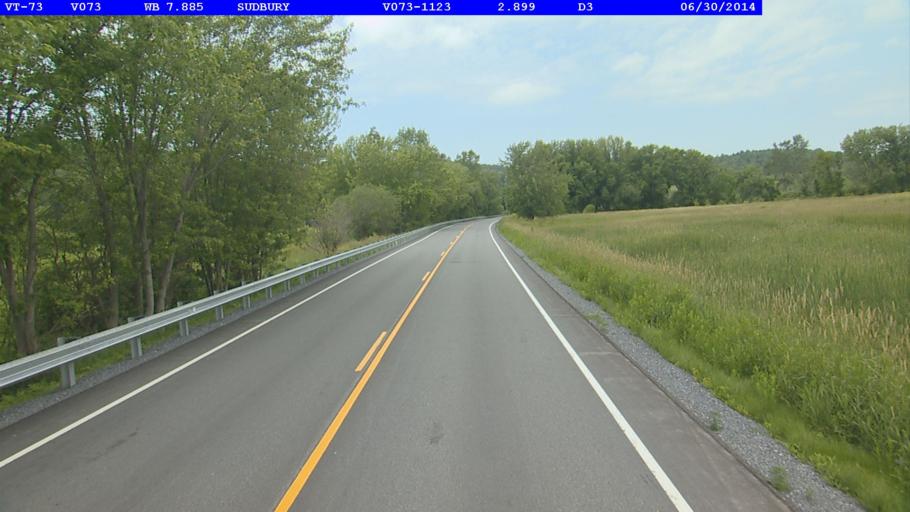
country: US
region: Vermont
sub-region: Rutland County
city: Brandon
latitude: 43.8095
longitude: -73.1517
